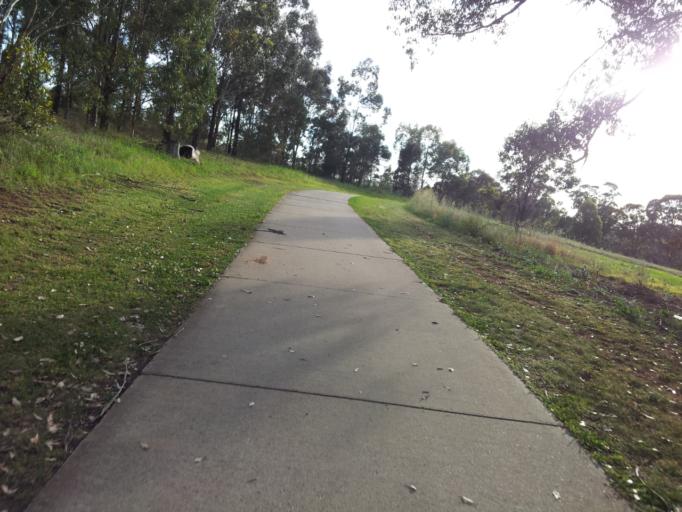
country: AU
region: New South Wales
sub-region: Fairfield
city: Horsley Park
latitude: -33.8541
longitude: 150.8707
